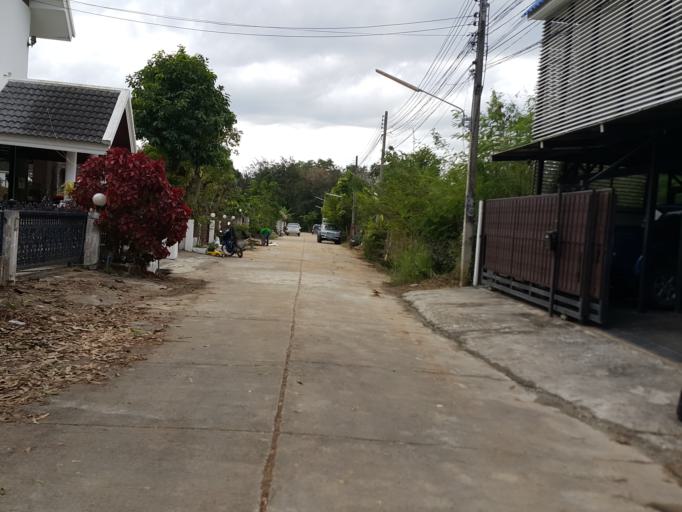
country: TH
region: Chiang Mai
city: San Sai
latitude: 18.8643
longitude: 99.1142
